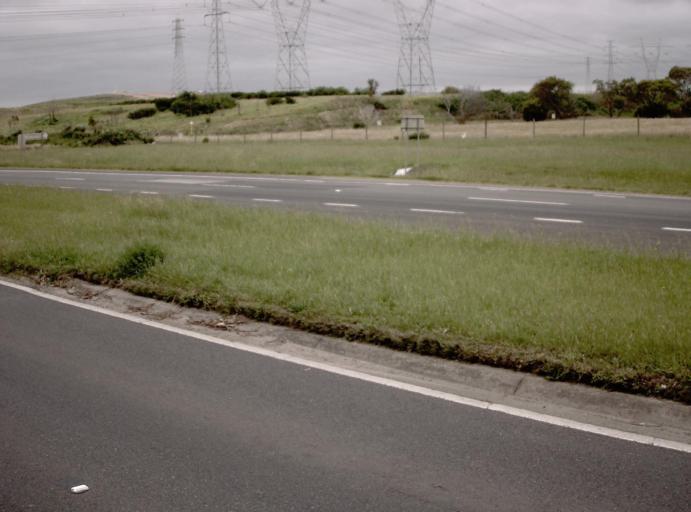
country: AU
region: Victoria
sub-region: Casey
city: Lynbrook
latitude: -38.0657
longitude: 145.2659
